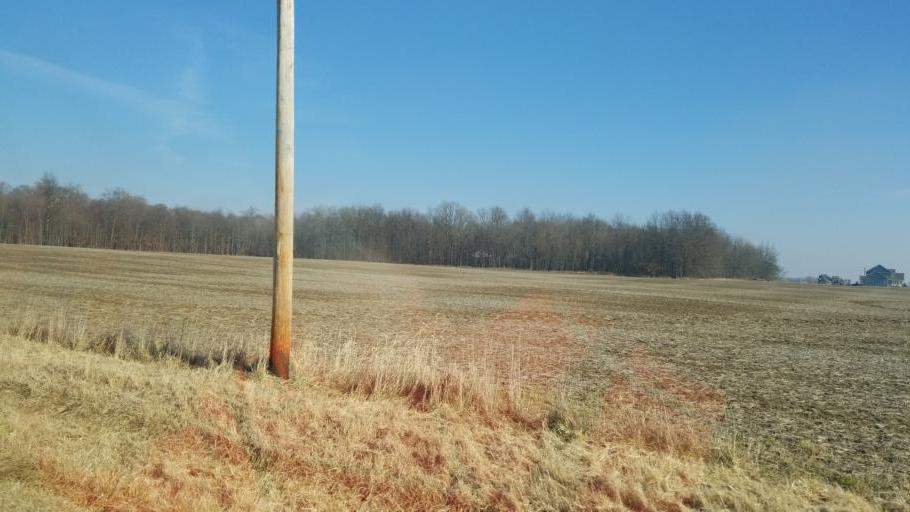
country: US
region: Ohio
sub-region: Seneca County
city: Tiffin
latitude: 40.9951
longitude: -83.0742
